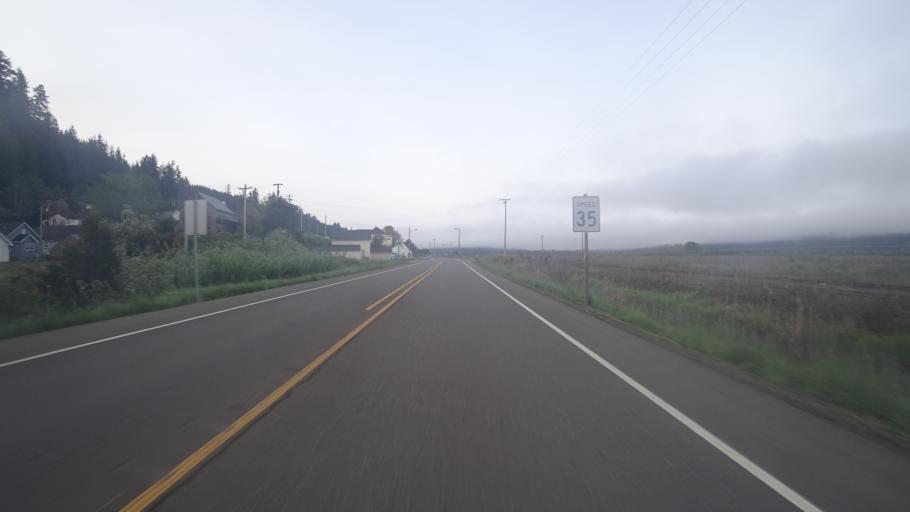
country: US
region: Oregon
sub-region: Douglas County
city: Reedsport
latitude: 43.7348
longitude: -124.1115
